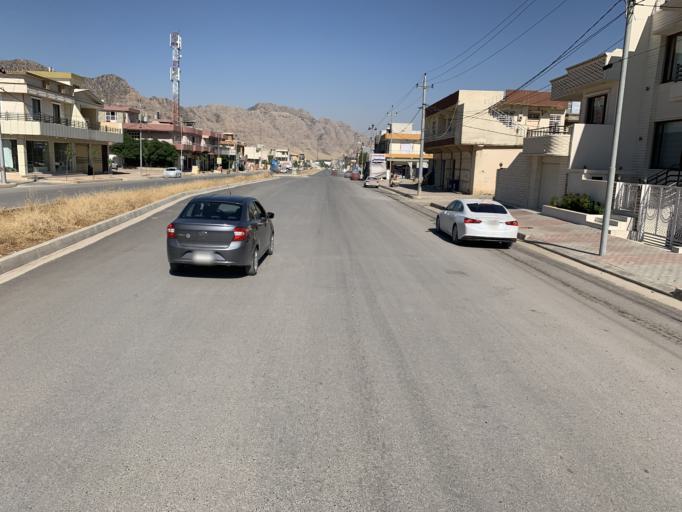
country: IQ
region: As Sulaymaniyah
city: Raniye
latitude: 36.2593
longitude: 44.8637
